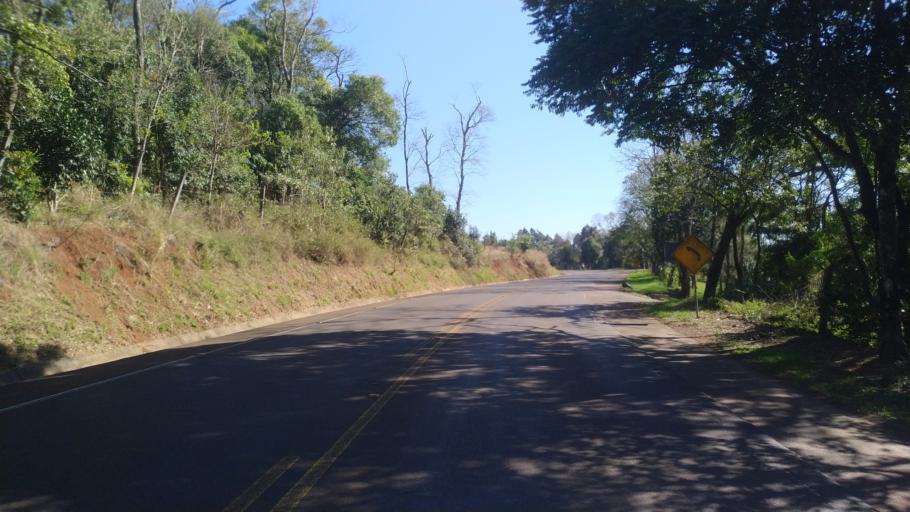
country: BR
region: Santa Catarina
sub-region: Chapeco
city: Chapeco
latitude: -27.1554
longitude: -52.6157
